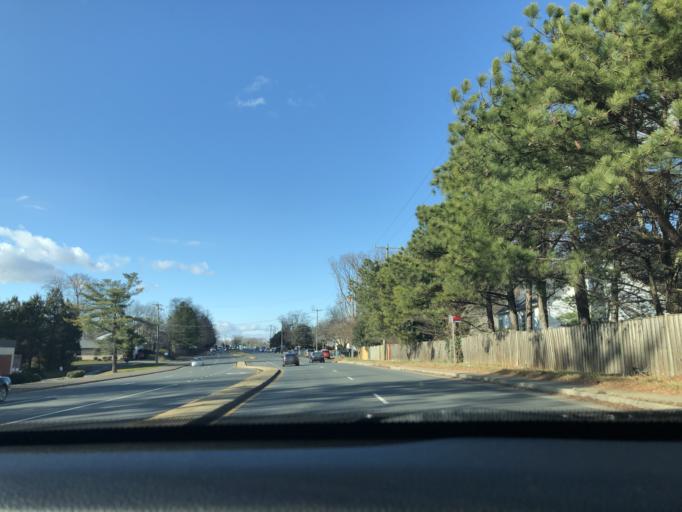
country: US
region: Virginia
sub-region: Fairfax County
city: Burke
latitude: 38.8151
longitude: -77.2700
